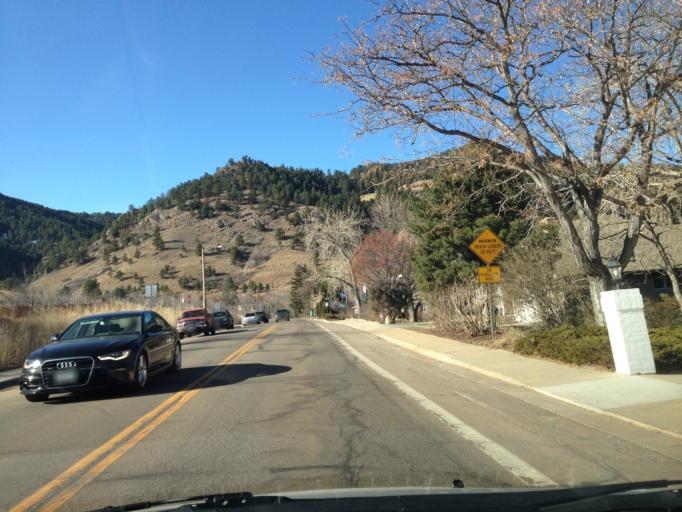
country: US
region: Colorado
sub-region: Boulder County
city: Boulder
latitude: 40.0001
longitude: -105.2857
